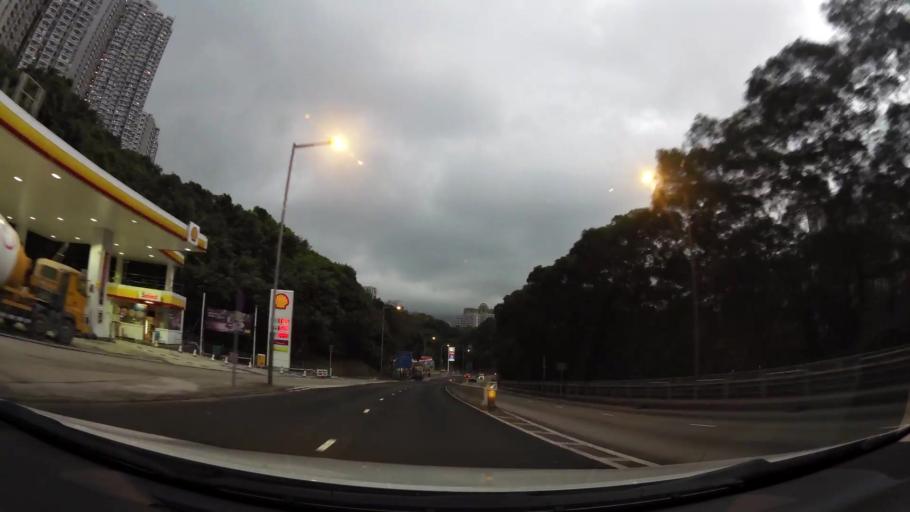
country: HK
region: Tsuen Wan
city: Tsuen Wan
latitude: 22.3558
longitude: 114.0998
